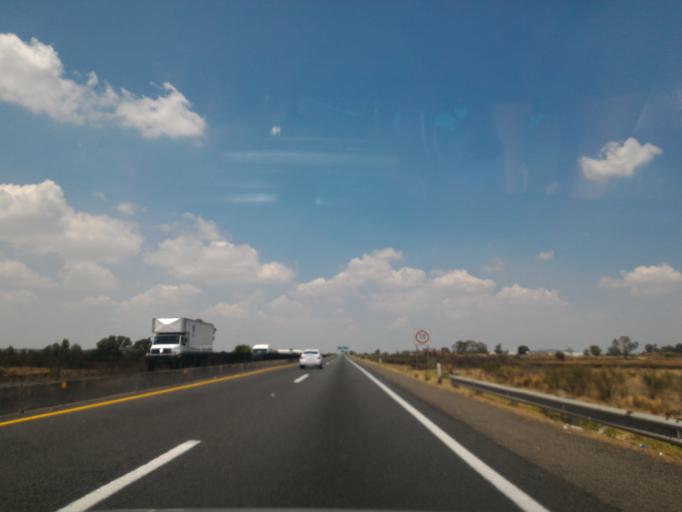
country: MX
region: Jalisco
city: Tepatitlan de Morelos
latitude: 20.8833
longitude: -102.7283
